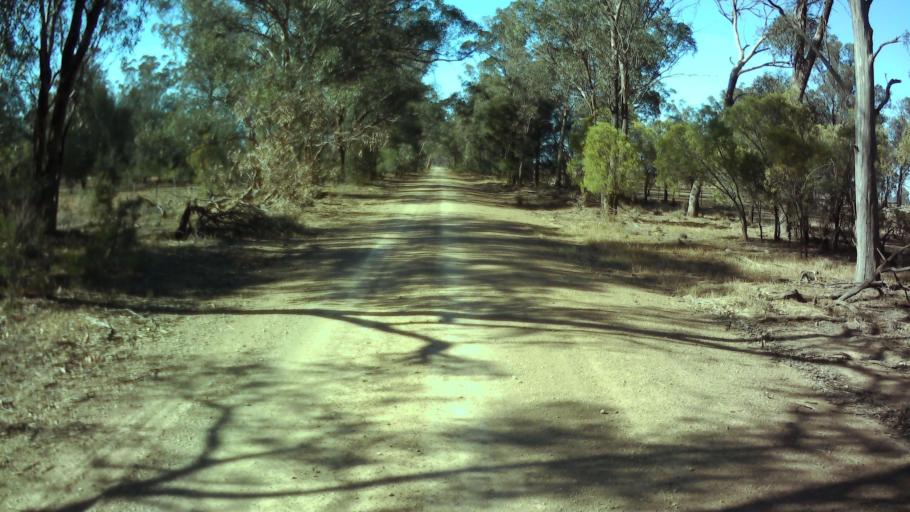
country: AU
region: New South Wales
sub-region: Weddin
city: Grenfell
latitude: -33.9389
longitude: 147.8713
